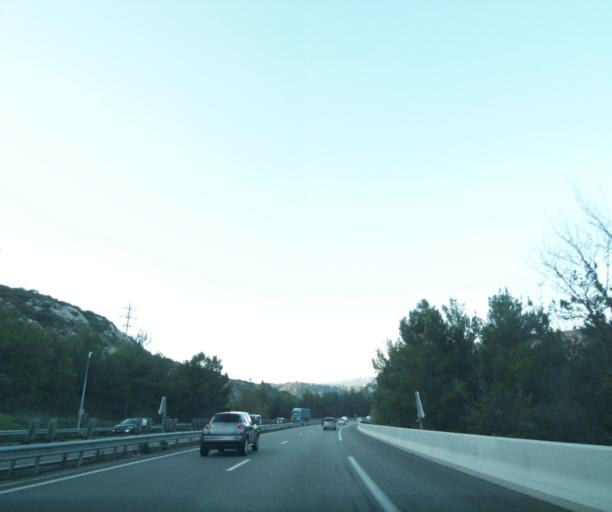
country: FR
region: Provence-Alpes-Cote d'Azur
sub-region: Departement des Bouches-du-Rhone
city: Roquevaire
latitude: 43.3604
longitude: 5.6151
